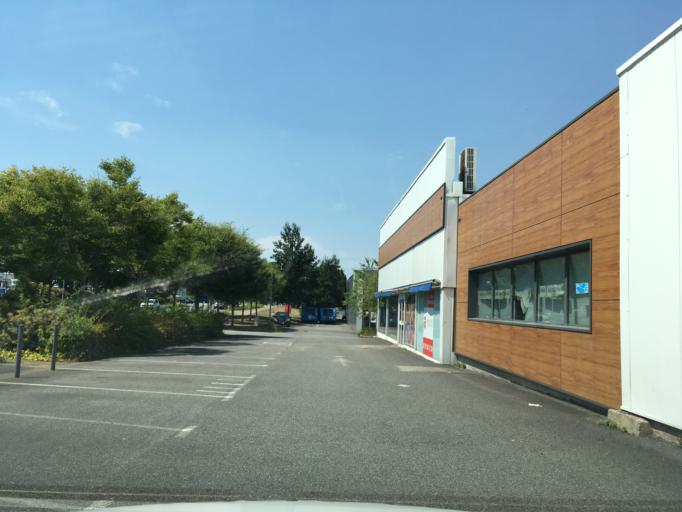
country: FR
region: Brittany
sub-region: Departement du Morbihan
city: Queven
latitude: 47.7630
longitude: -3.3975
